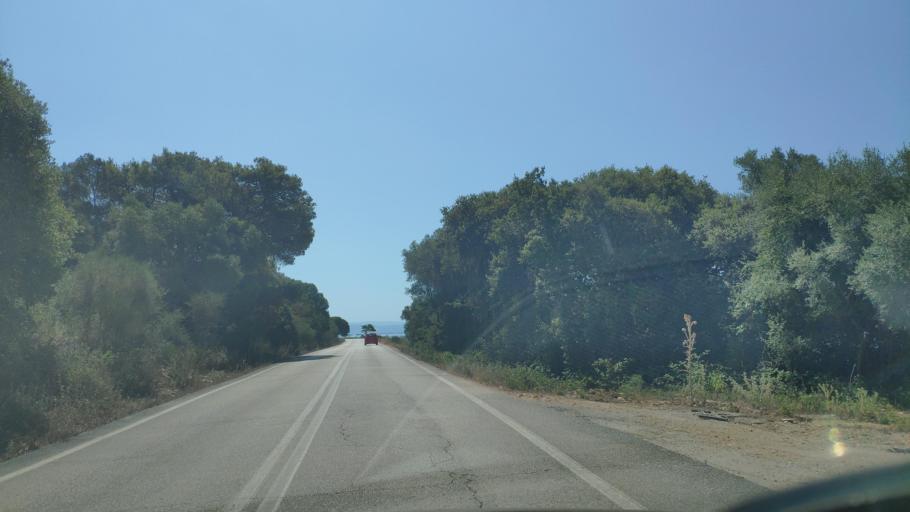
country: GR
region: Epirus
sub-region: Nomos Artas
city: Aneza
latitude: 39.0329
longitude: 20.8608
